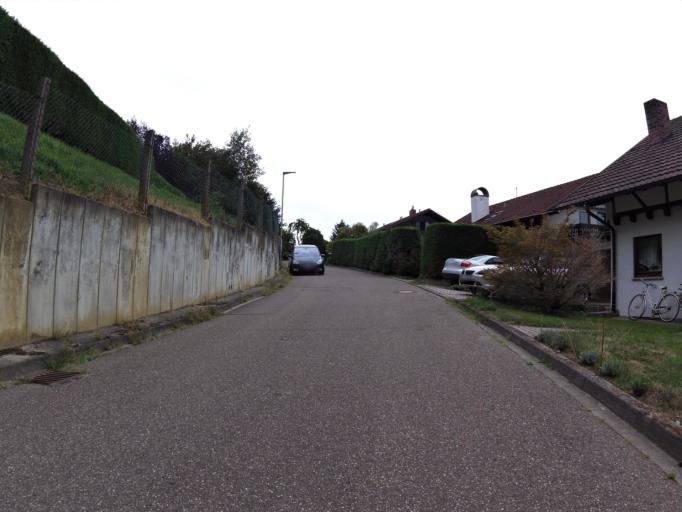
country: DE
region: Baden-Wuerttemberg
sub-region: Freiburg Region
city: Hohberg
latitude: 48.3417
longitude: 7.9028
